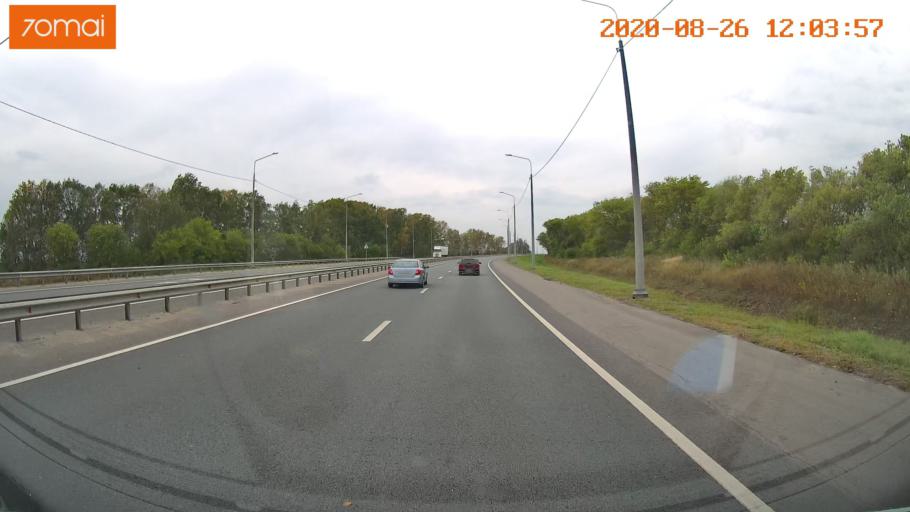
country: RU
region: Rjazan
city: Kiritsy
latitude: 54.3047
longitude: 40.1969
